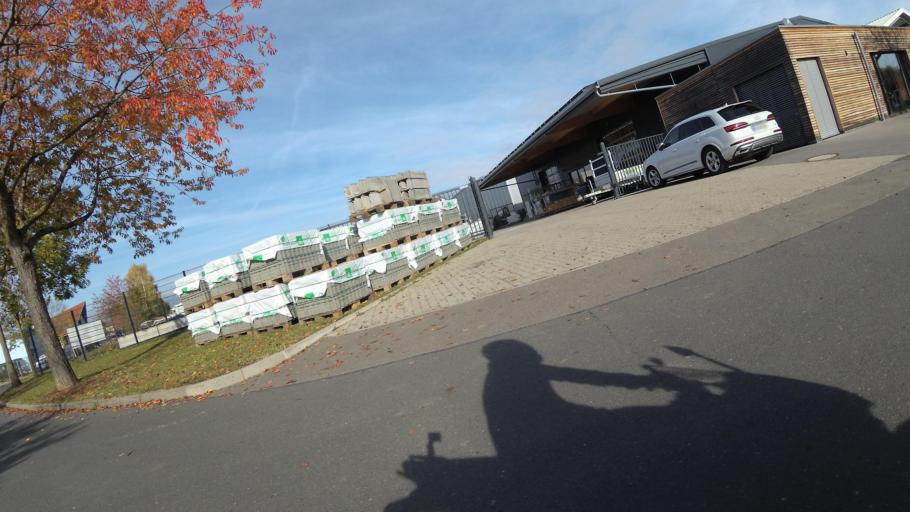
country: DE
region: Baden-Wuerttemberg
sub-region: Regierungsbezirk Stuttgart
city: Oedheim
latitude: 49.2458
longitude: 9.2491
